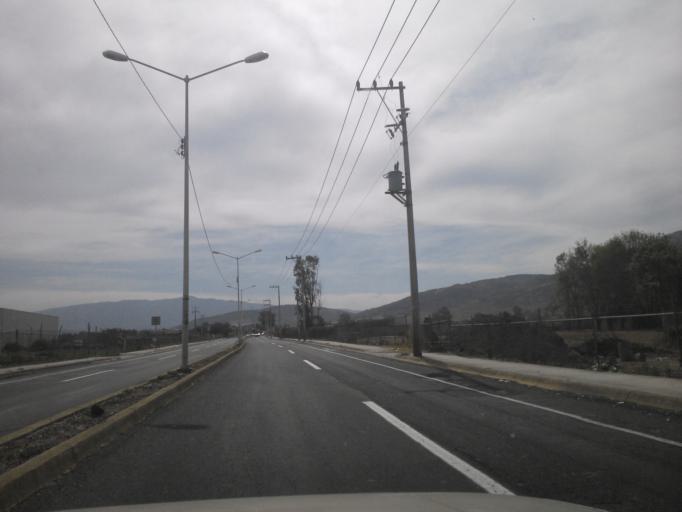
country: MX
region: Jalisco
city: San Sebastian el Grande
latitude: 20.5199
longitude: -103.4099
